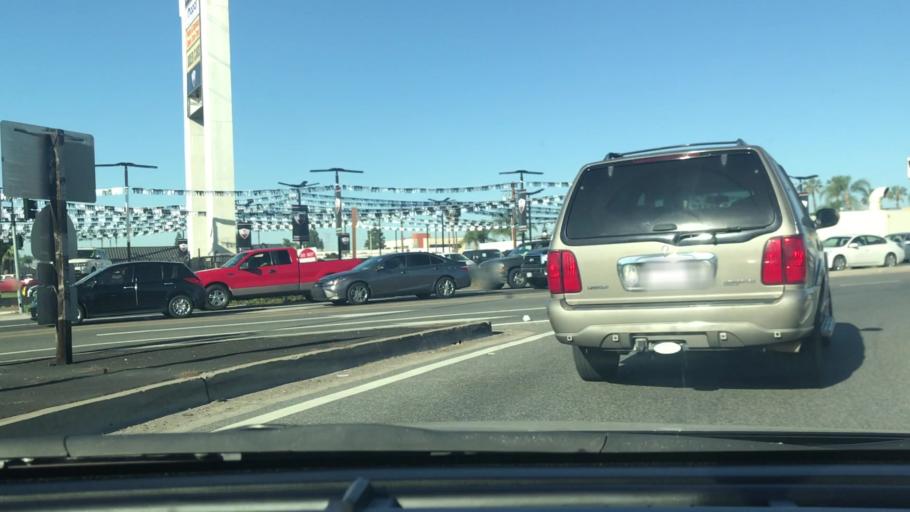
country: US
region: California
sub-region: Orange County
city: Placentia
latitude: 33.8613
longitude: -117.8784
